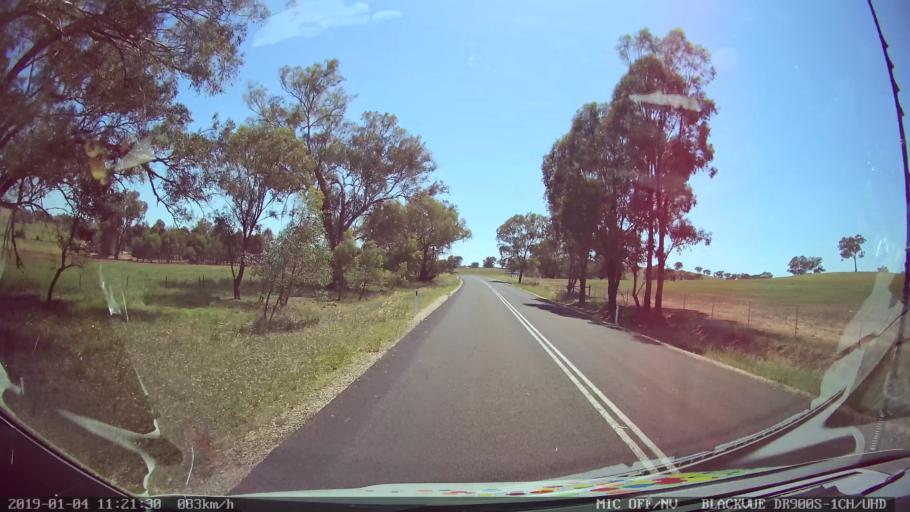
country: AU
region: New South Wales
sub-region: Cabonne
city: Molong
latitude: -33.1540
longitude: 148.7119
